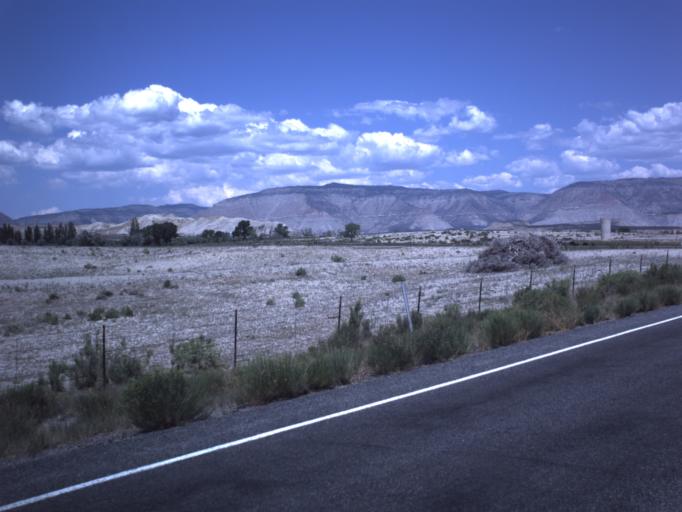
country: US
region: Utah
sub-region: Emery County
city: Orangeville
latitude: 39.2048
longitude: -111.0479
